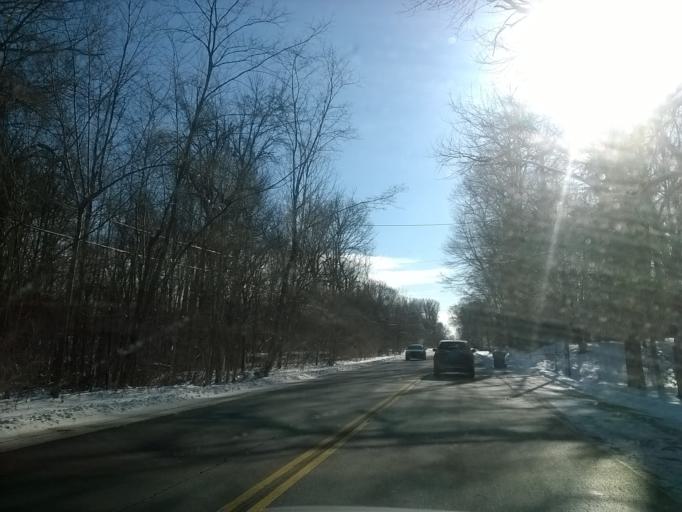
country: US
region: Indiana
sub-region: Hamilton County
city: Carmel
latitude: 39.9503
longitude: -86.1268
